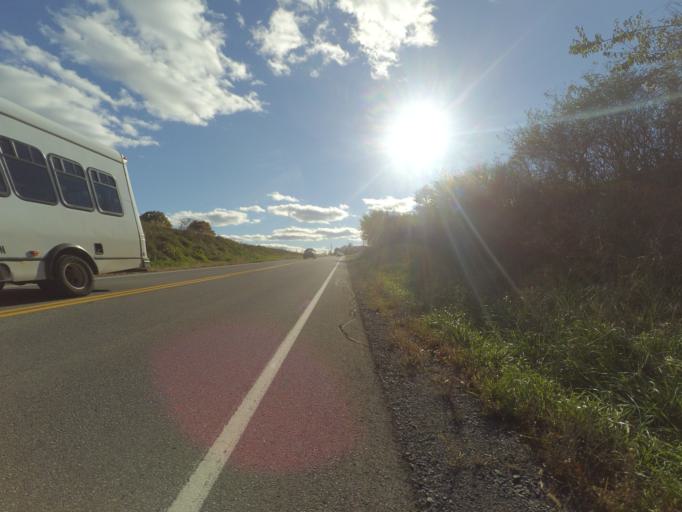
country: US
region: Pennsylvania
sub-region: Centre County
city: Pleasant Gap
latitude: 40.8563
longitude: -77.7872
